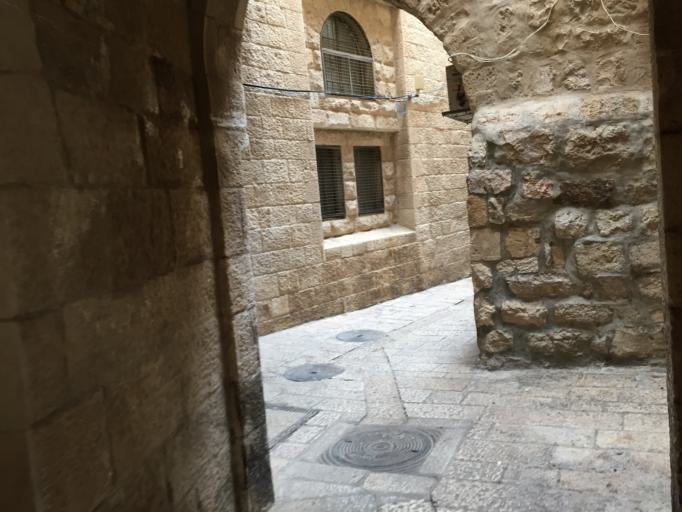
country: PS
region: West Bank
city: Old City
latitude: 31.7762
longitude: 35.2322
